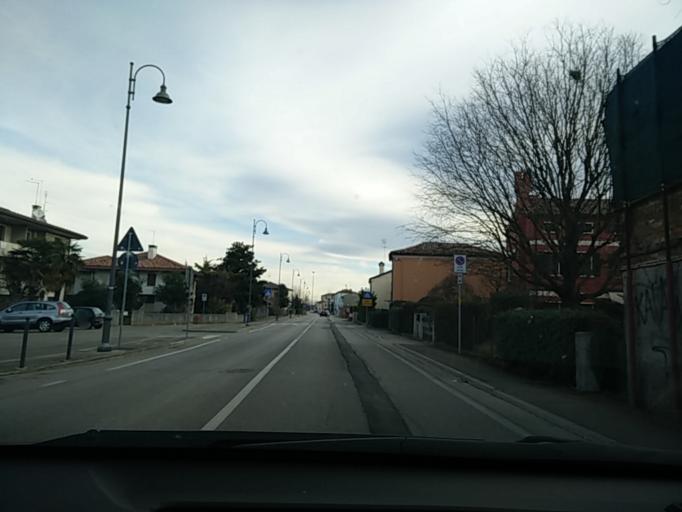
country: IT
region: Veneto
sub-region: Provincia di Venezia
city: Noventa di Piave
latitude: 45.6647
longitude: 12.5326
